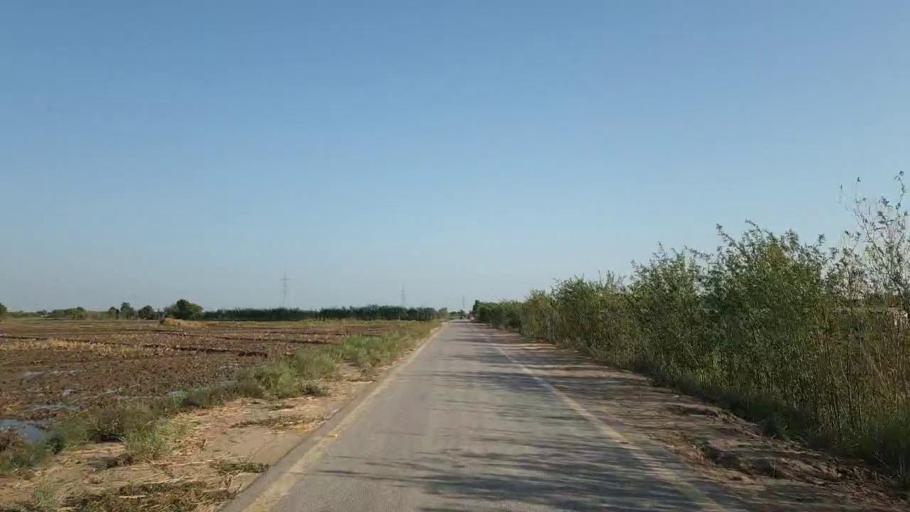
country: PK
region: Sindh
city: Hyderabad
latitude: 25.3532
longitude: 68.4124
